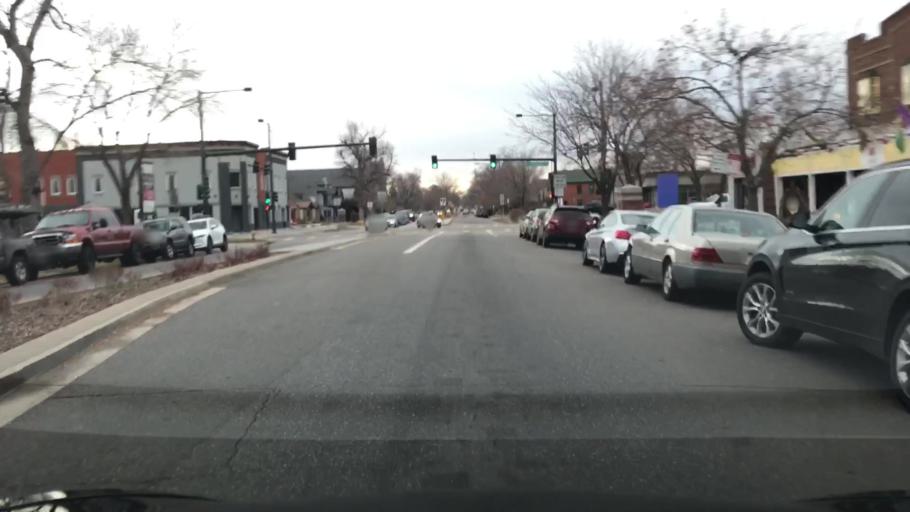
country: US
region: Colorado
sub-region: Denver County
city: Denver
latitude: 39.7118
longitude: -104.9829
